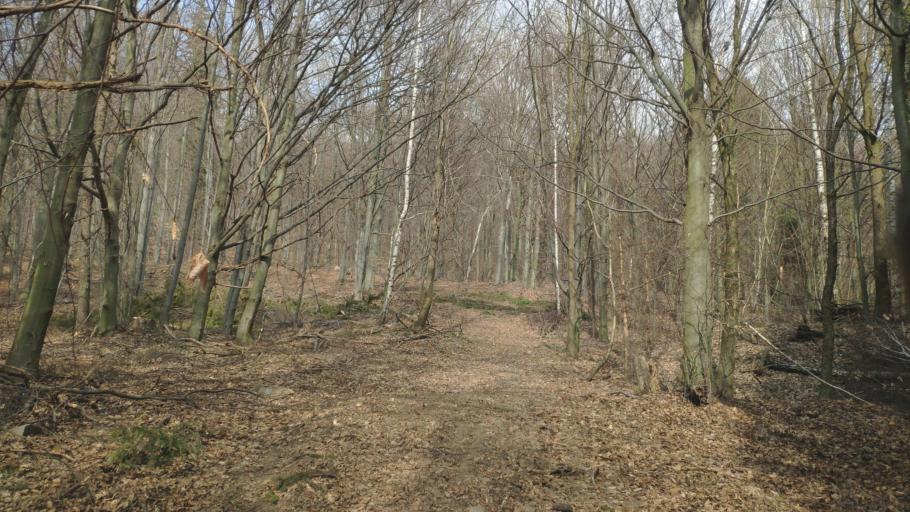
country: SK
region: Kosicky
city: Moldava nad Bodvou
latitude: 48.7439
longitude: 21.0342
